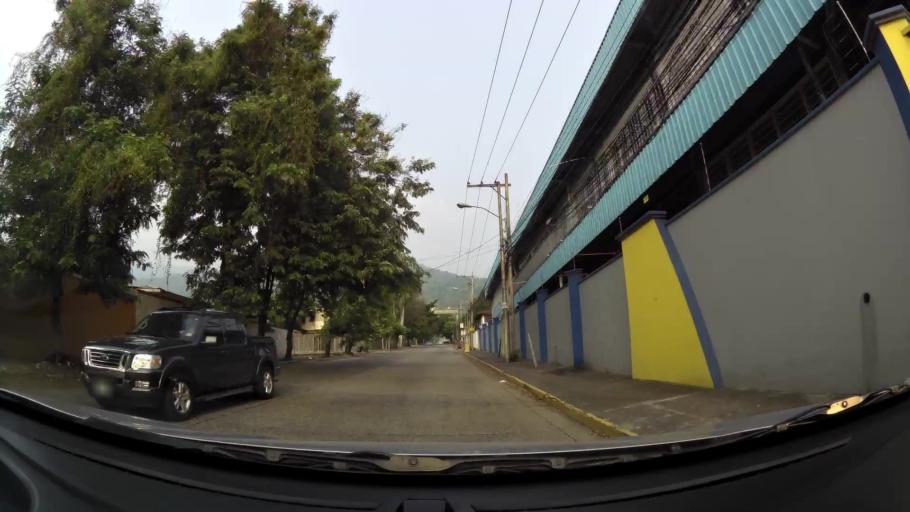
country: HN
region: Cortes
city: Armenta
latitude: 15.4983
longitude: -88.0427
